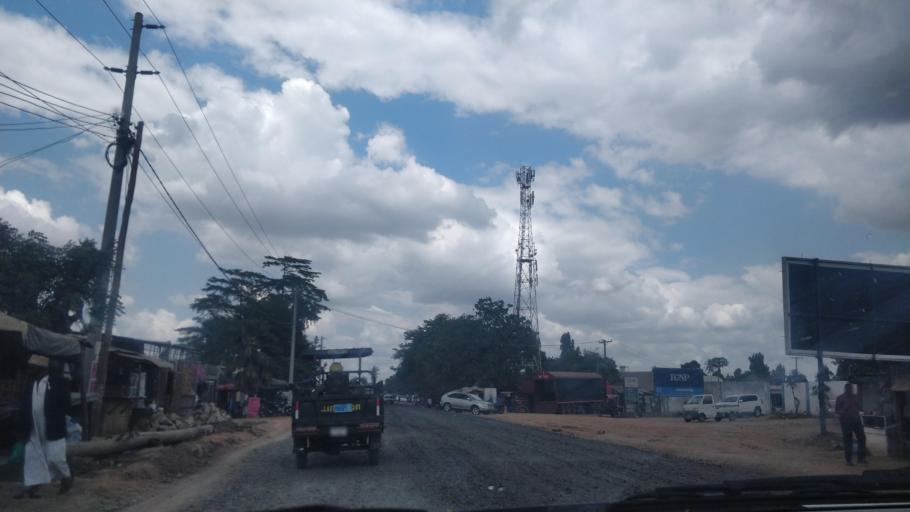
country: TZ
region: Dar es Salaam
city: Magomeni
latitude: -6.8059
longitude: 39.2234
